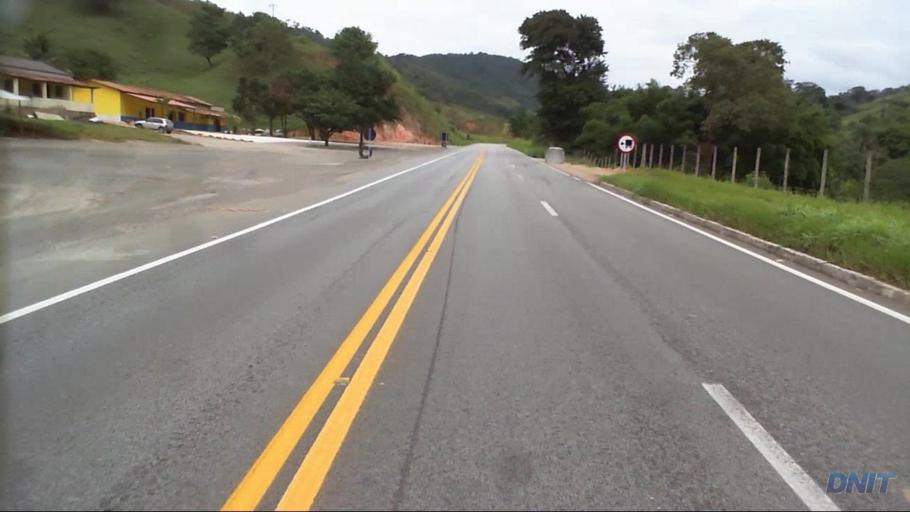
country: BR
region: Minas Gerais
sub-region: Timoteo
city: Timoteo
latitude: -19.6193
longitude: -42.8517
